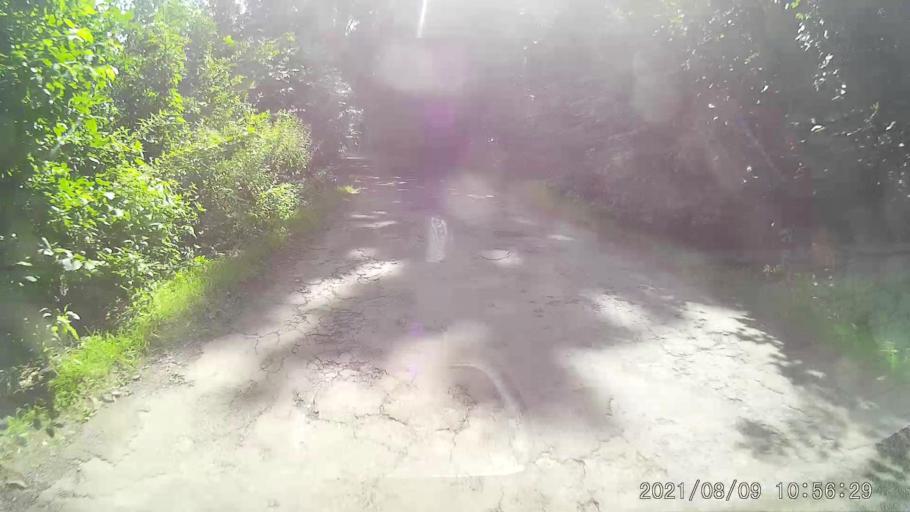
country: PL
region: Lower Silesian Voivodeship
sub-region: Powiat klodzki
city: Polanica-Zdroj
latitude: 50.4314
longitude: 16.5484
